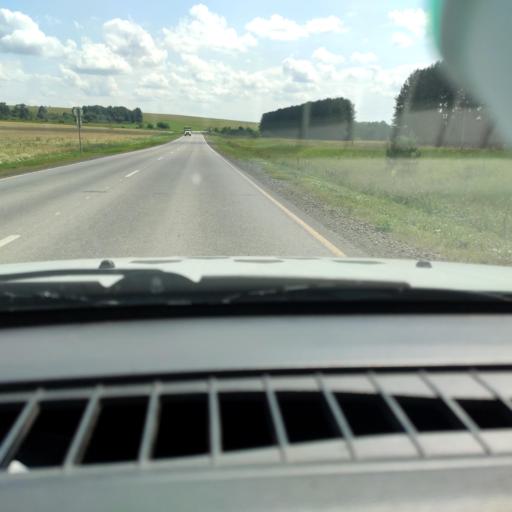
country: RU
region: Bashkortostan
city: Verkhniye Kigi
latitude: 55.3713
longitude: 58.6824
